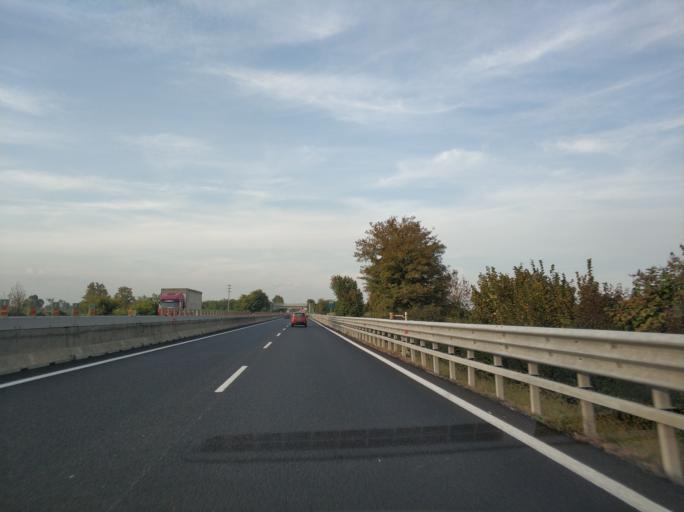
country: IT
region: Piedmont
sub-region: Provincia di Torino
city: Borgaro Torinese
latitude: 45.1540
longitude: 7.6872
